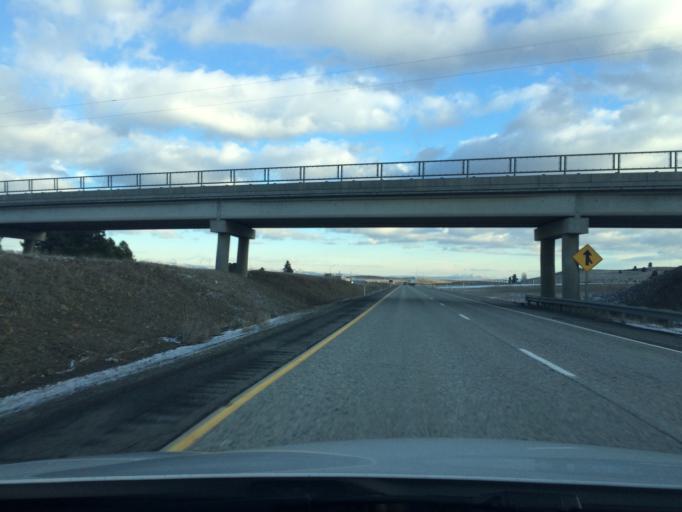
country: US
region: Washington
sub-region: Kittitas County
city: Cle Elum
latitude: 47.1147
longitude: -120.7916
